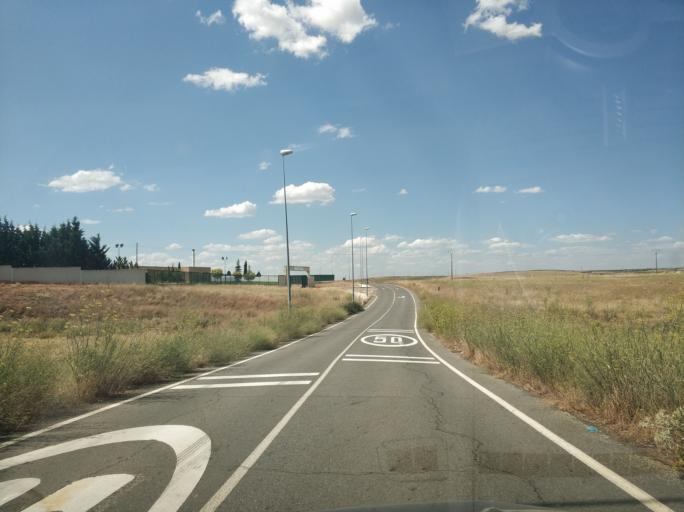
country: ES
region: Castille and Leon
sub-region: Provincia de Salamanca
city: Aldeatejada
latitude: 40.9464
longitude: -5.6931
